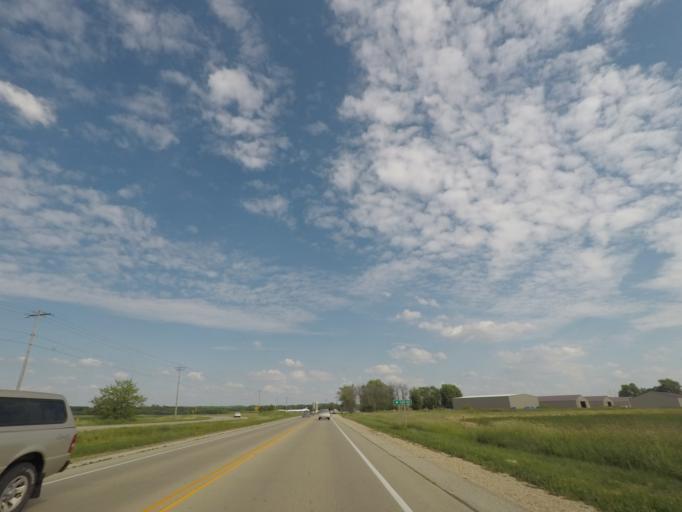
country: US
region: Wisconsin
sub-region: Walworth County
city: Whitewater
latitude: 42.8170
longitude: -88.6916
